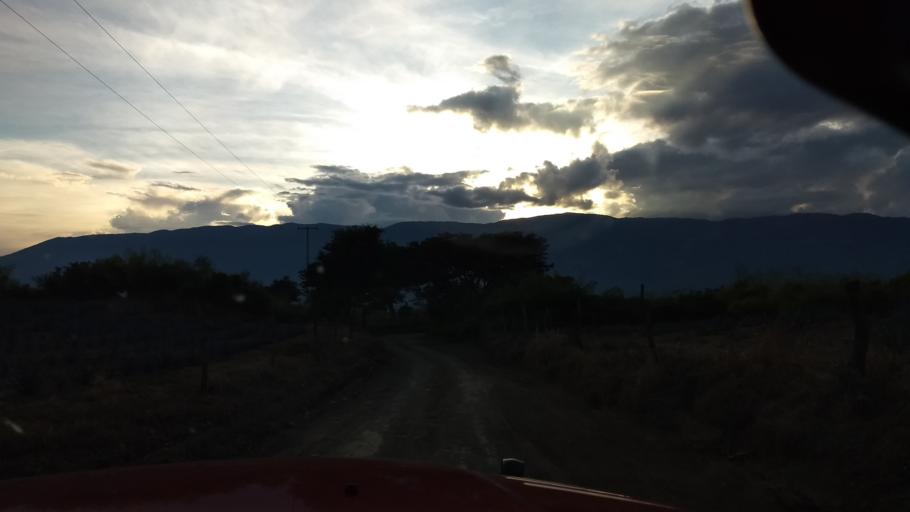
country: MX
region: Colima
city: Suchitlan
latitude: 19.4935
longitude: -103.7825
